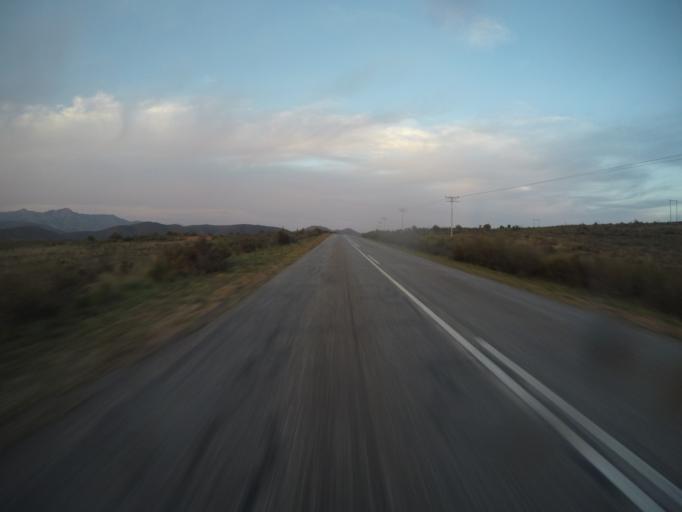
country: ZA
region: Western Cape
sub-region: Eden District Municipality
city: Plettenberg Bay
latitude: -33.7429
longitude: 23.4591
